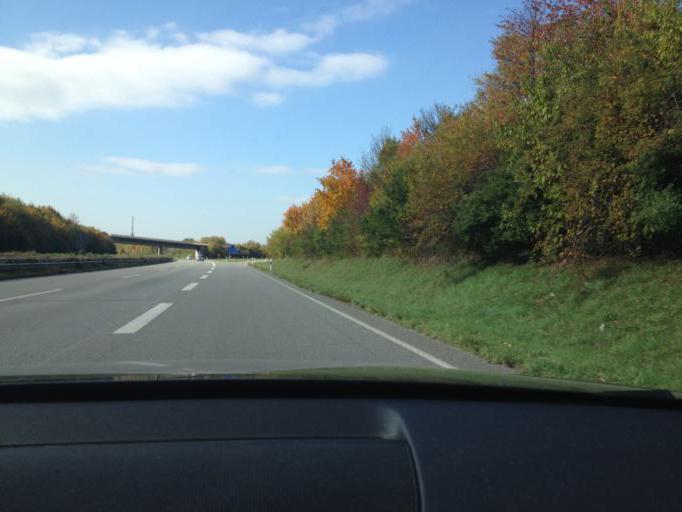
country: DE
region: Rheinland-Pfalz
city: Zweibrucken
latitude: 49.2348
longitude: 7.4019
